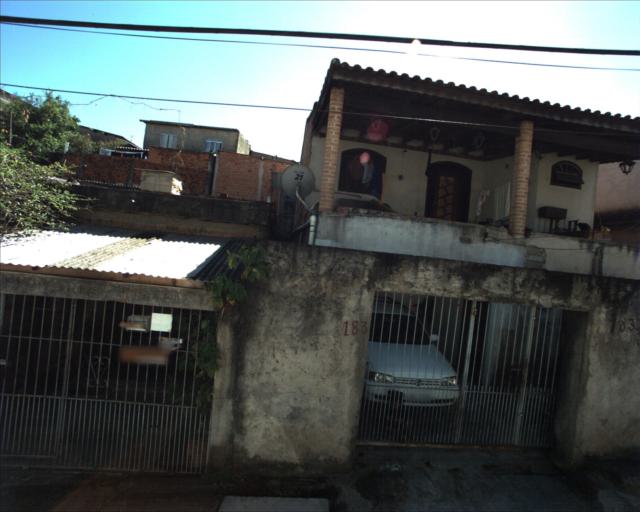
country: BR
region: Sao Paulo
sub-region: Votorantim
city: Votorantim
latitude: -23.5220
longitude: -47.4342
